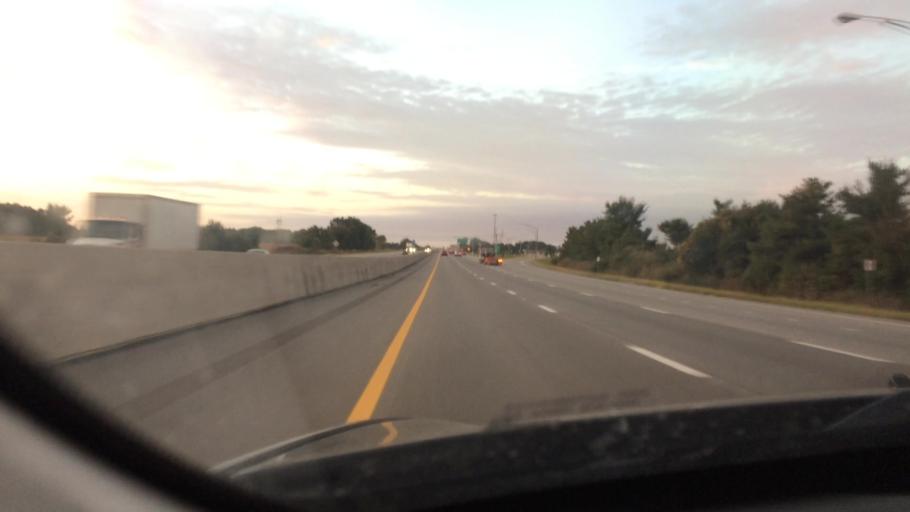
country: US
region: Ohio
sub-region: Hancock County
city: Findlay
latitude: 41.1066
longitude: -83.6599
